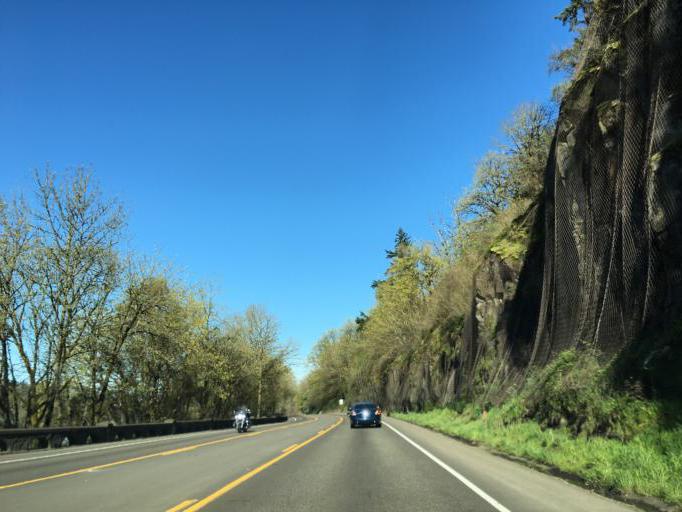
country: US
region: Oregon
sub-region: Clackamas County
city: Oregon City
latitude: 45.3443
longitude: -122.6302
